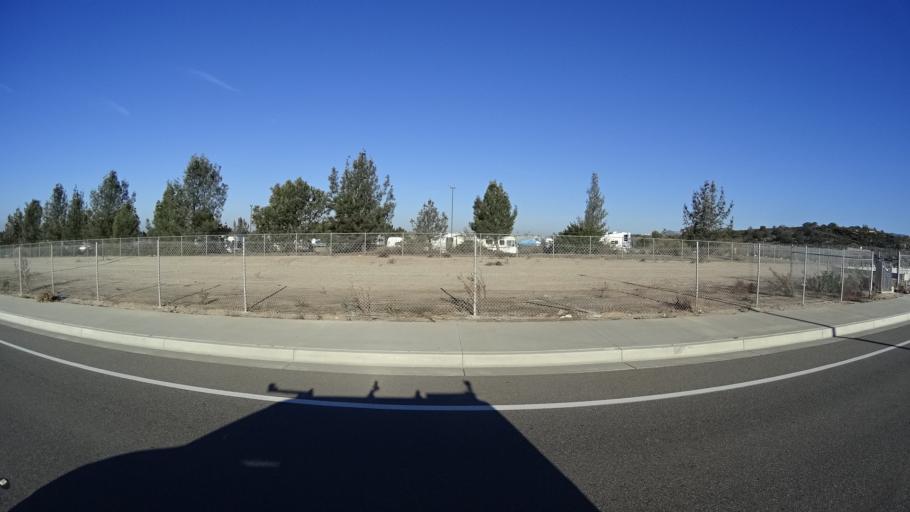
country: US
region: California
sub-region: Orange County
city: Lake Forest
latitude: 33.6662
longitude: -117.7013
